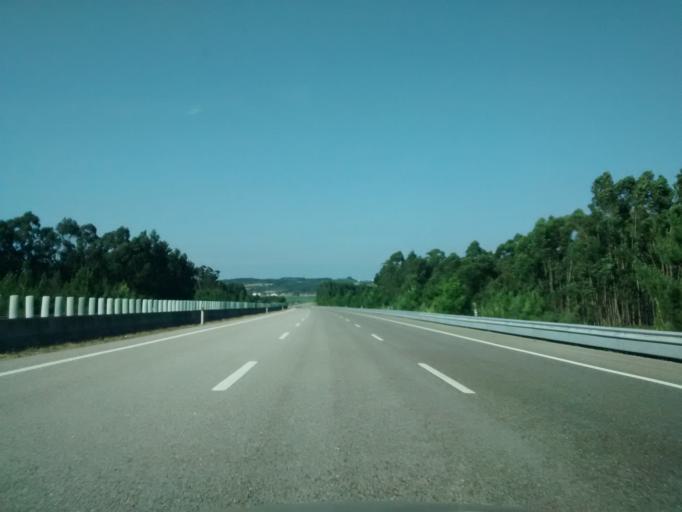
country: PT
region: Coimbra
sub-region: Figueira da Foz
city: Lavos
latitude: 40.0825
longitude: -8.7687
